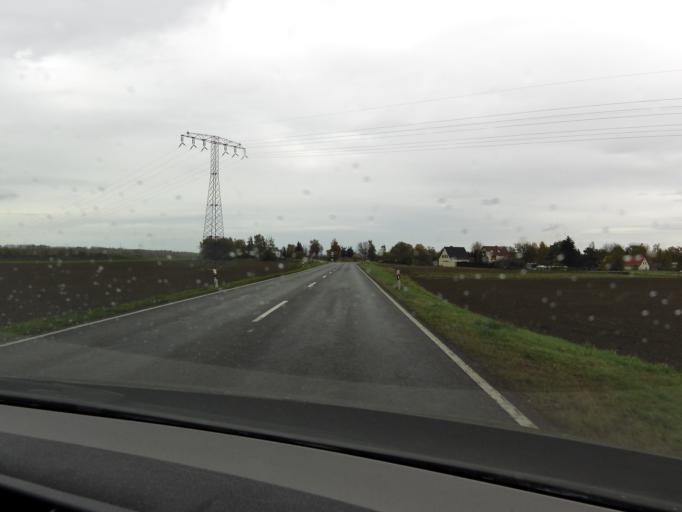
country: DE
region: Saxony
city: Elstertrebnitz
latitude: 51.1324
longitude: 12.2205
